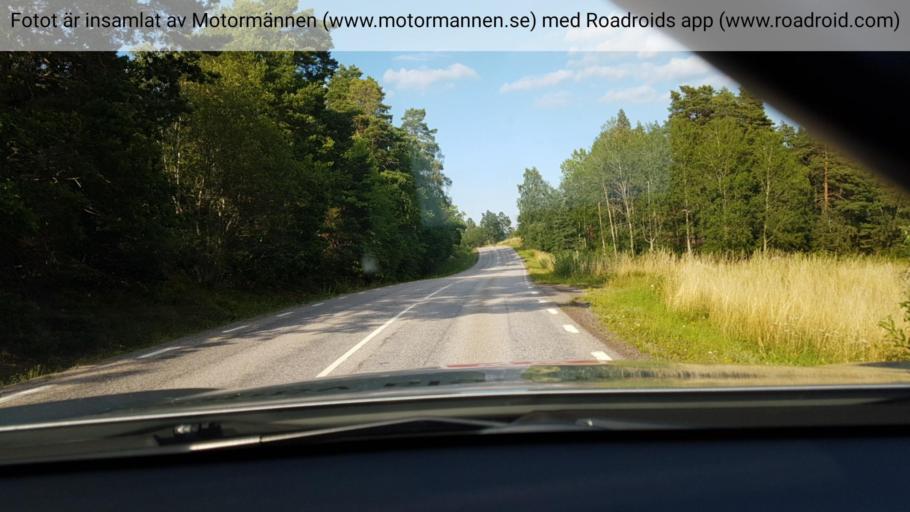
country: SE
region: Vaestra Goetaland
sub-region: Lidkopings Kommun
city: Lidkoping
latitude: 58.6431
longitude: 13.1479
